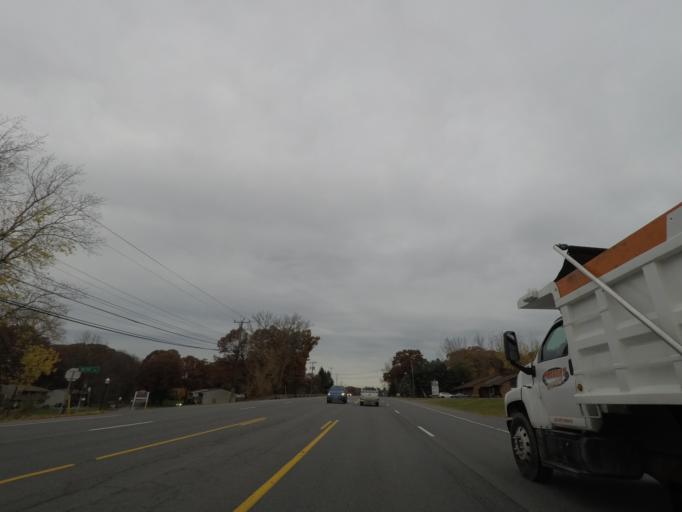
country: US
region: New York
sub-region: Saratoga County
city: Country Knolls
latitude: 42.8787
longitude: -73.7740
